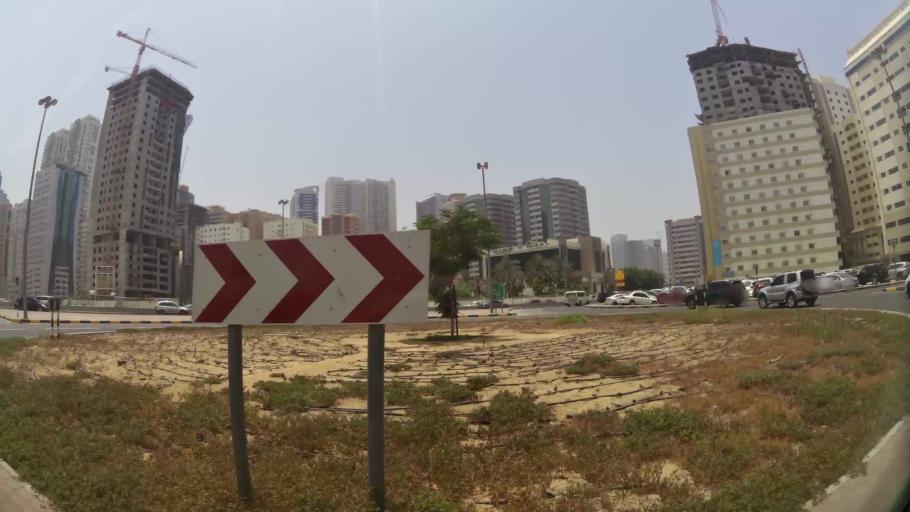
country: AE
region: Ash Shariqah
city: Sharjah
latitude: 25.3154
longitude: 55.3811
